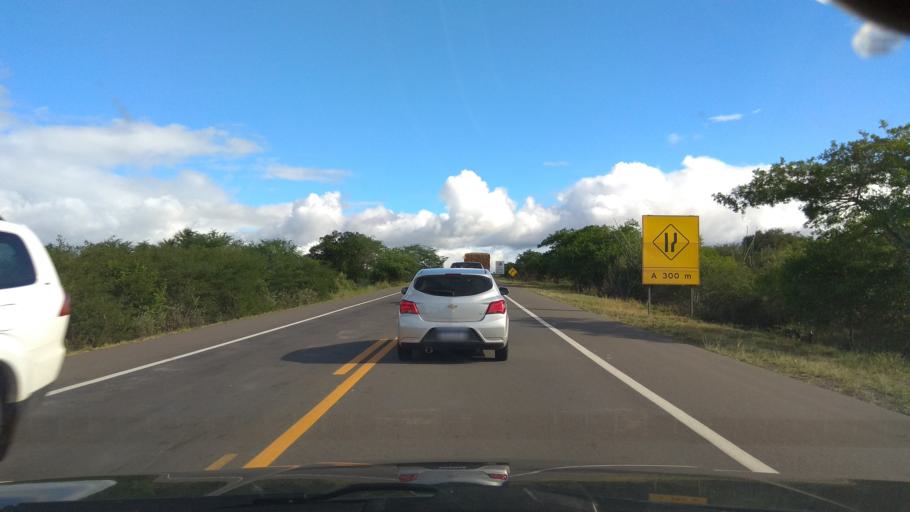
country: BR
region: Bahia
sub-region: Castro Alves
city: Castro Alves
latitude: -12.6457
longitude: -39.6048
